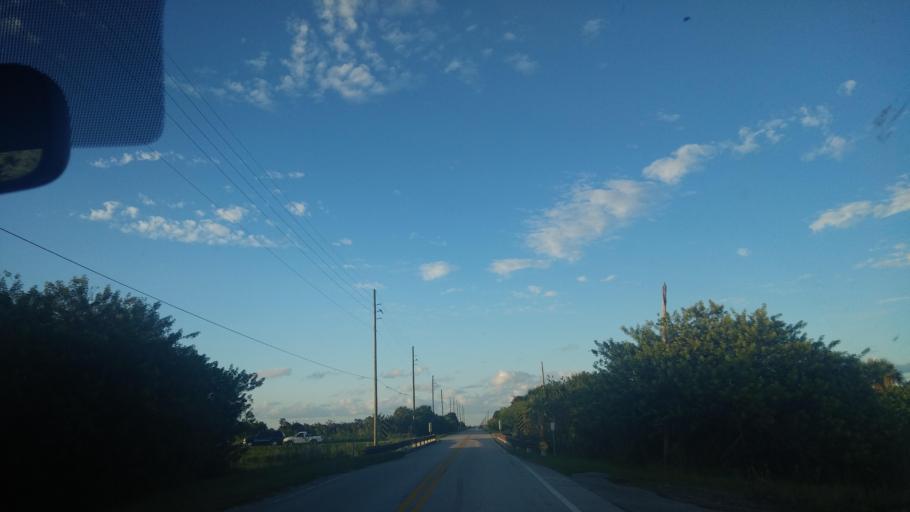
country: US
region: Florida
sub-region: Indian River County
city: Fellsmere
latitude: 27.6950
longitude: -80.6429
